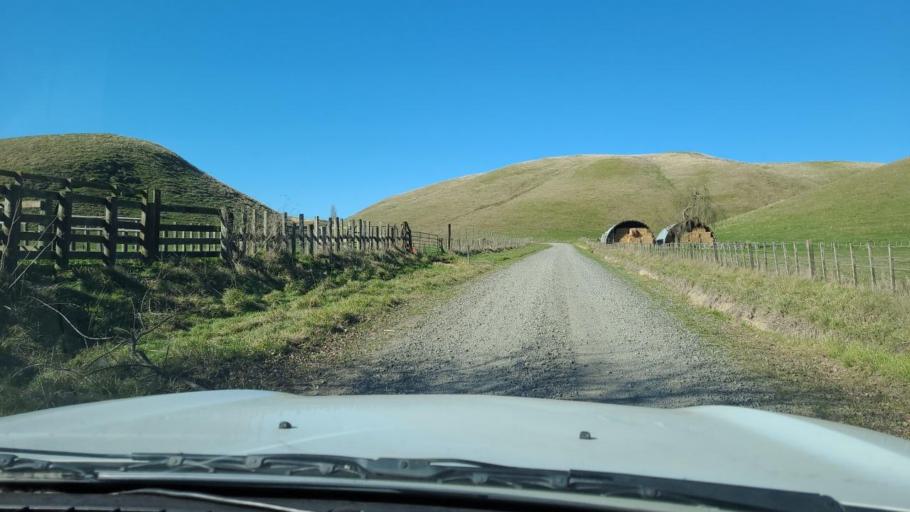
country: NZ
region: Hawke's Bay
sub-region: Hastings District
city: Hastings
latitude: -39.7616
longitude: 176.7972
